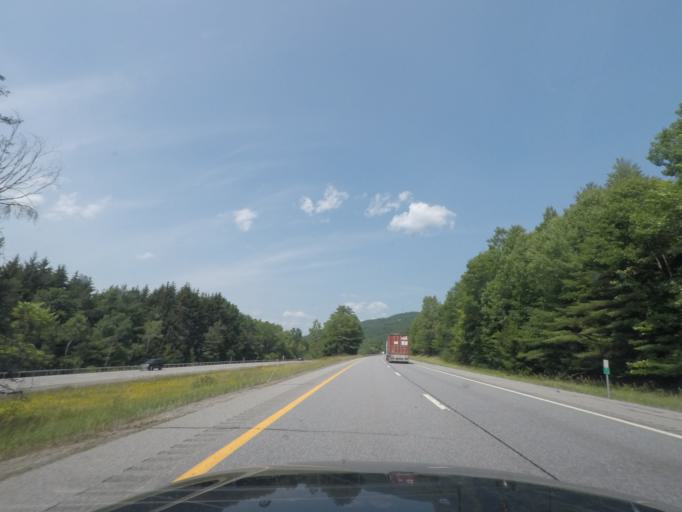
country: US
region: New York
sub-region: Warren County
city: Warrensburg
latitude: 43.5589
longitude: -73.7332
